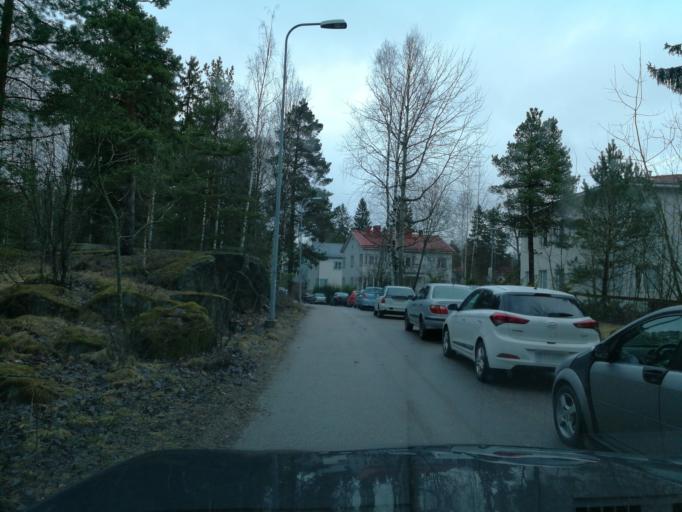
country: FI
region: Uusimaa
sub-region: Helsinki
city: Helsinki
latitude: 60.2196
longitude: 24.9554
